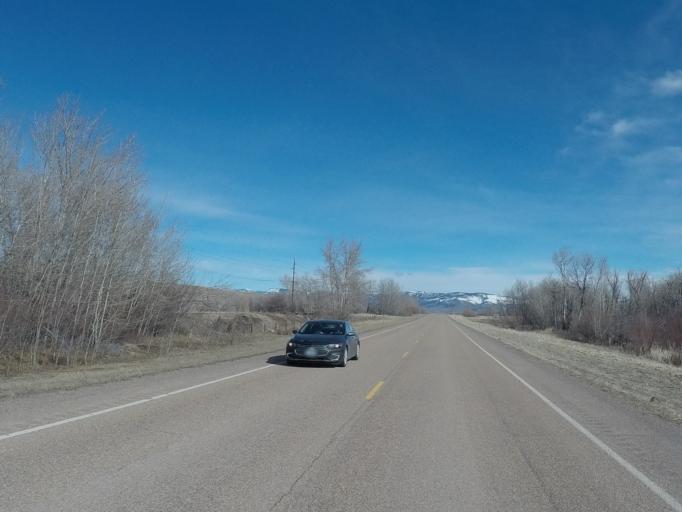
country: US
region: Montana
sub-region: Granite County
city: Philipsburg
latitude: 46.5302
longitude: -113.2235
